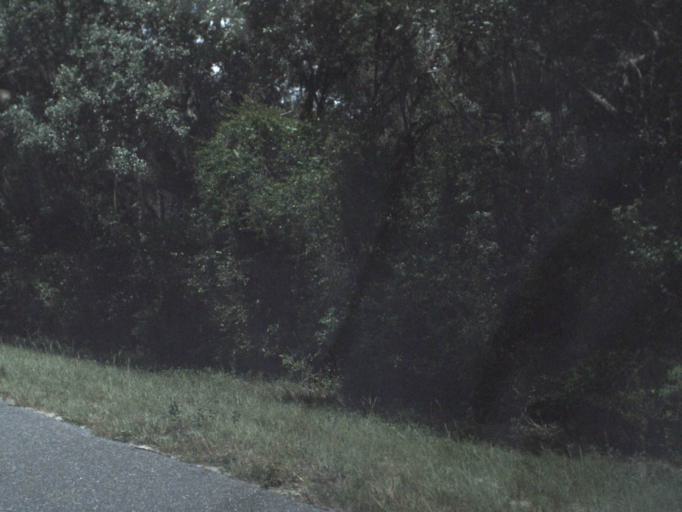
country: US
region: Florida
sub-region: Gilchrist County
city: Trenton
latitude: 29.7413
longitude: -82.7405
